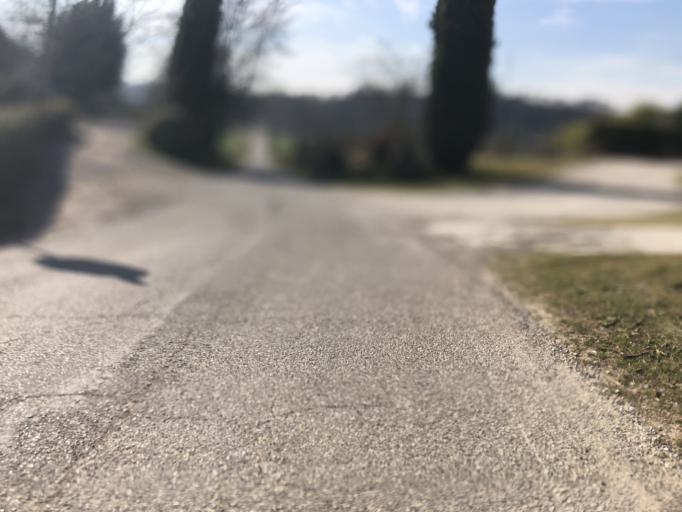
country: IT
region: Veneto
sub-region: Provincia di Verona
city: San Giorgio in Salici
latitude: 45.3934
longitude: 10.7657
